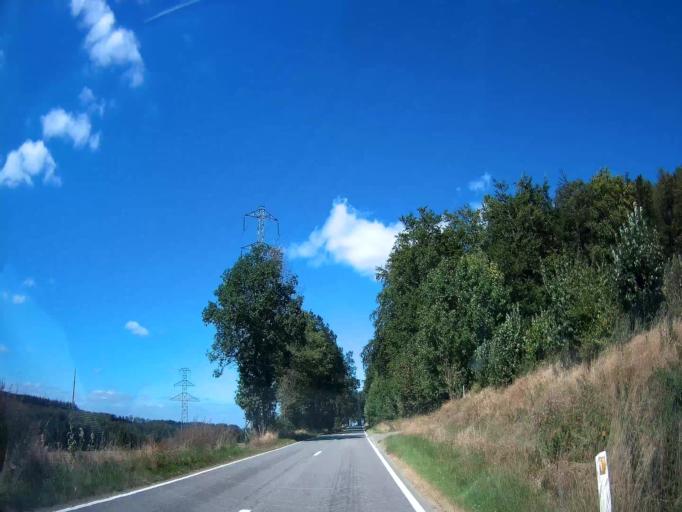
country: BE
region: Wallonia
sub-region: Province du Luxembourg
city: La Roche-en-Ardenne
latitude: 50.1598
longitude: 5.6051
